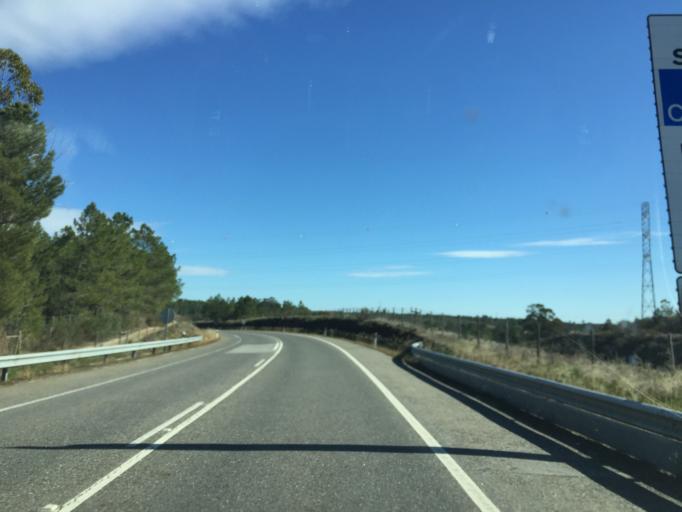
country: ES
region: Extremadura
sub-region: Provincia de Caceres
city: Cedillo
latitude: 39.7326
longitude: -7.6719
